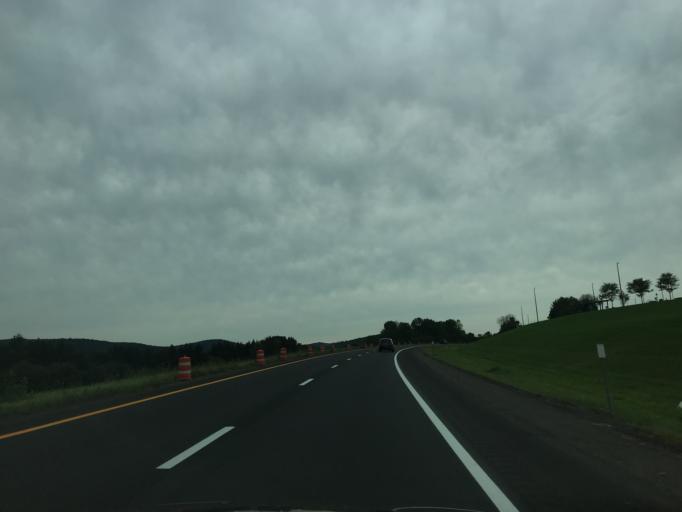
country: US
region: Pennsylvania
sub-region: Susquehanna County
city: Hallstead
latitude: 42.0185
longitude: -75.7788
